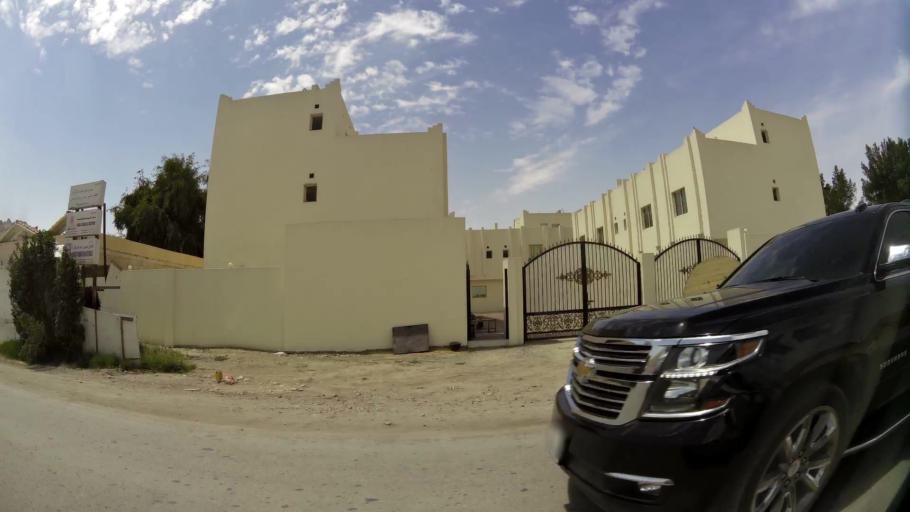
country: QA
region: Baladiyat ar Rayyan
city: Ar Rayyan
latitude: 25.2750
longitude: 51.4261
